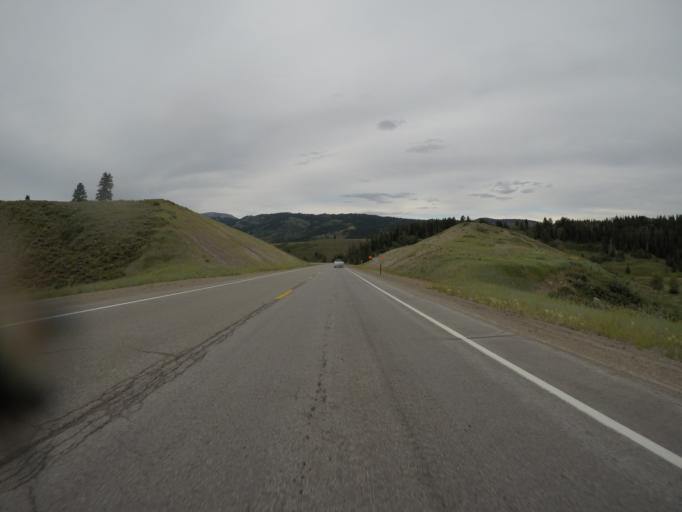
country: US
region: Wyoming
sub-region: Lincoln County
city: Afton
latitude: 42.5180
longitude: -110.9026
